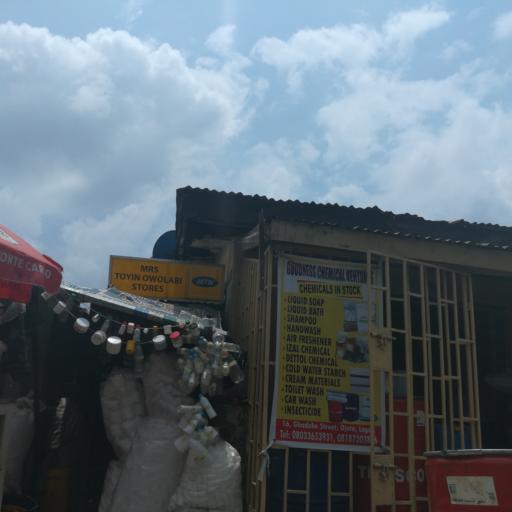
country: NG
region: Lagos
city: Ojota
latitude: 6.5867
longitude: 3.3804
